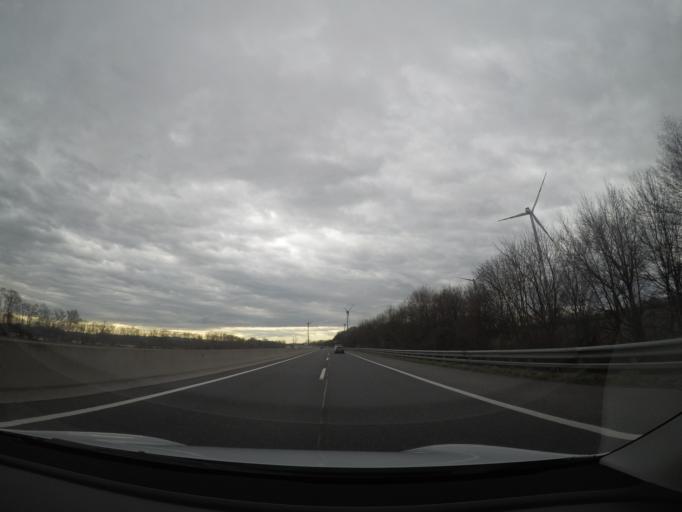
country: AT
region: Lower Austria
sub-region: Politischer Bezirk Baden
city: Ebreichsdorf
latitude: 47.9514
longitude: 16.3678
